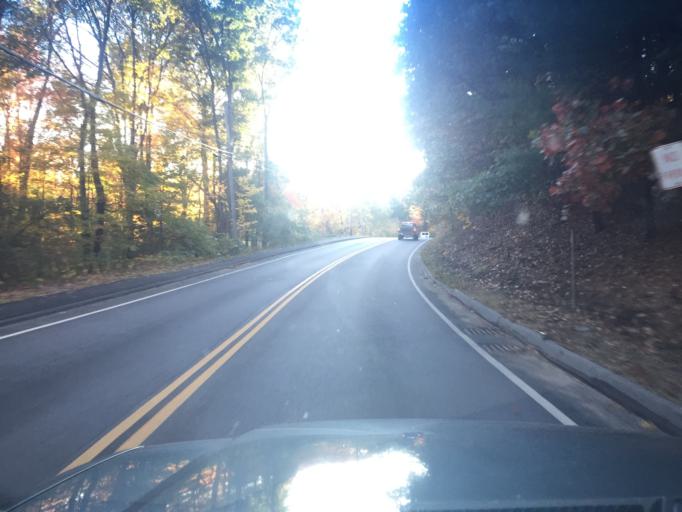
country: US
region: Massachusetts
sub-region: Middlesex County
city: Hudson
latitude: 42.3783
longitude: -71.5515
